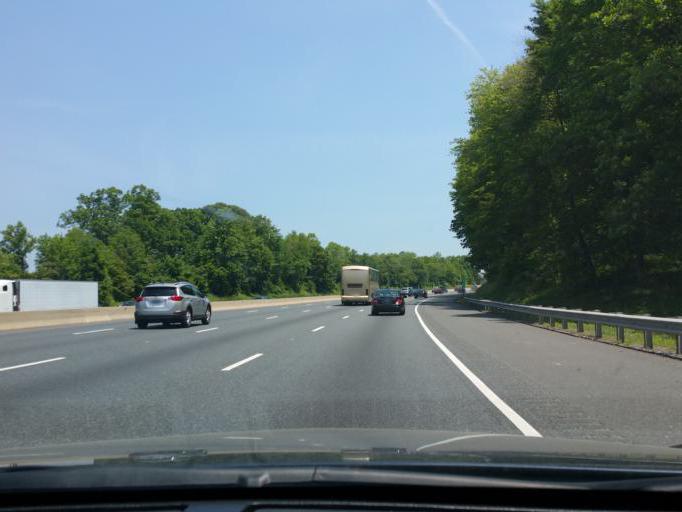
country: US
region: Maryland
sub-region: Baltimore County
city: Kingsville
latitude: 39.4168
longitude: -76.4086
